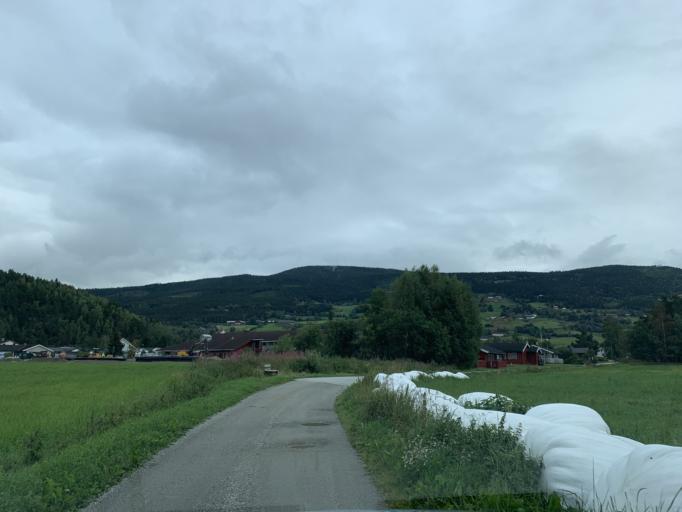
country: NO
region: Oppland
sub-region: Ringebu
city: Ringebu
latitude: 61.5272
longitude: 10.1267
